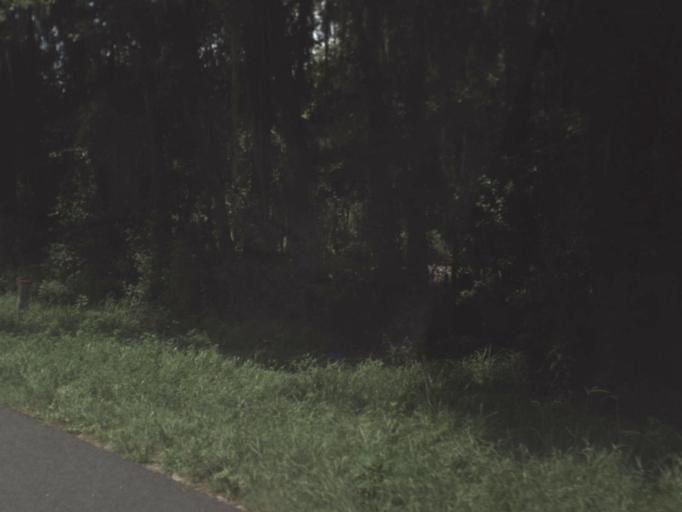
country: US
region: Florida
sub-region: Suwannee County
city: Wellborn
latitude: 30.3634
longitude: -82.7904
